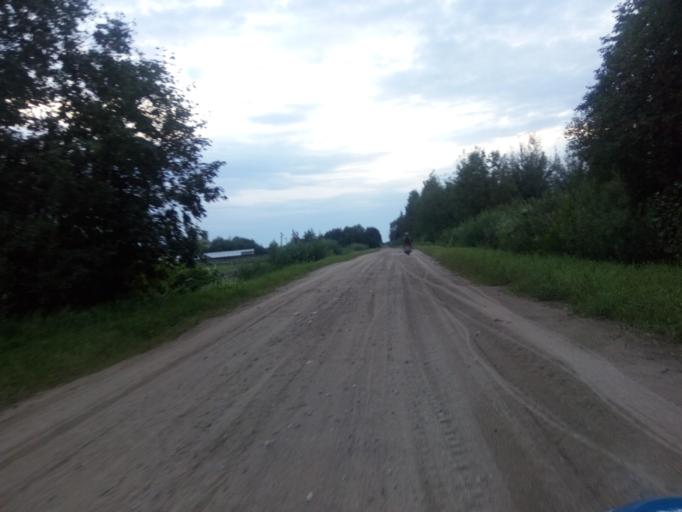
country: BY
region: Vitebsk
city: Dzisna
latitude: 55.6722
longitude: 28.3081
